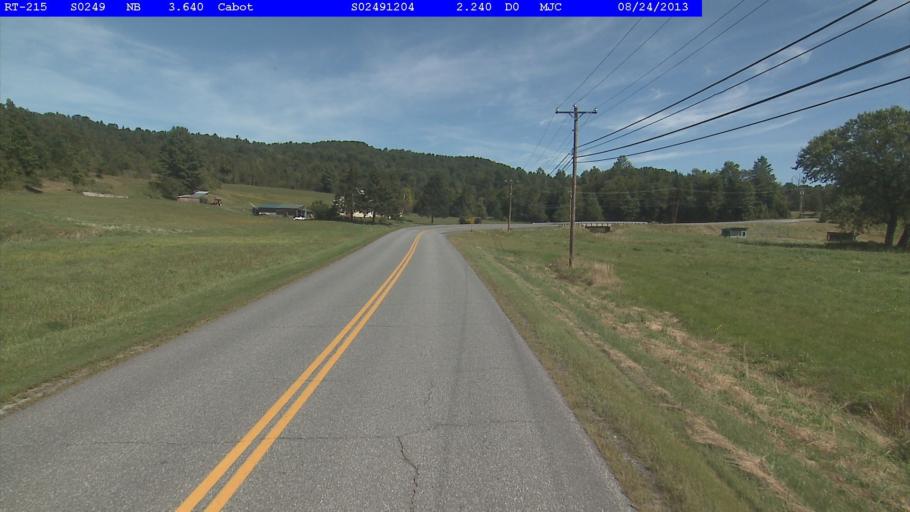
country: US
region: Vermont
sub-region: Caledonia County
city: Hardwick
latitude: 44.3974
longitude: -72.3257
